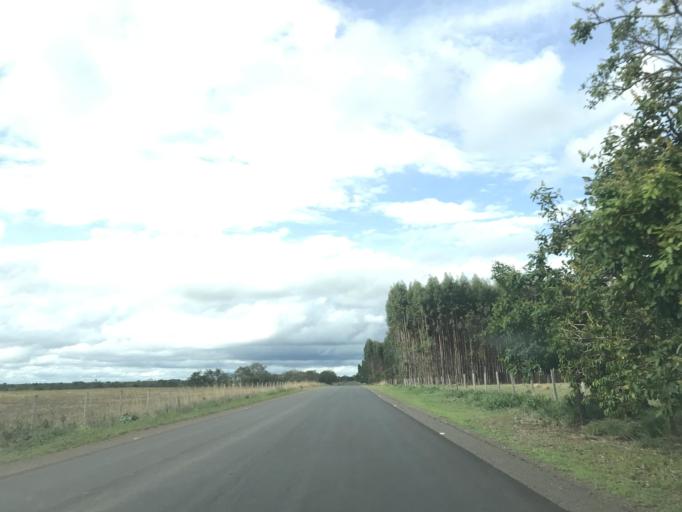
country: BR
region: Goias
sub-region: Bela Vista De Goias
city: Bela Vista de Goias
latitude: -16.9908
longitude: -48.6693
